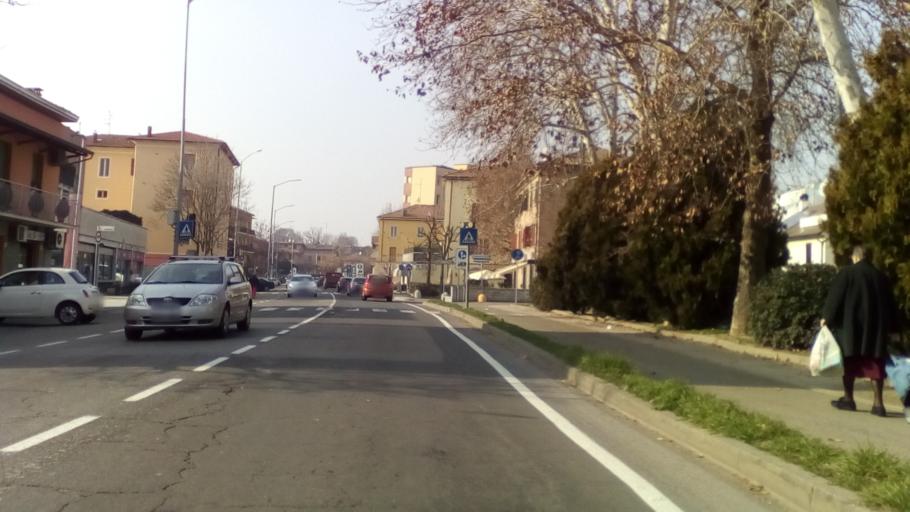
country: IT
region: Emilia-Romagna
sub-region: Provincia di Modena
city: Modena
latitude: 44.6287
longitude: 10.9452
